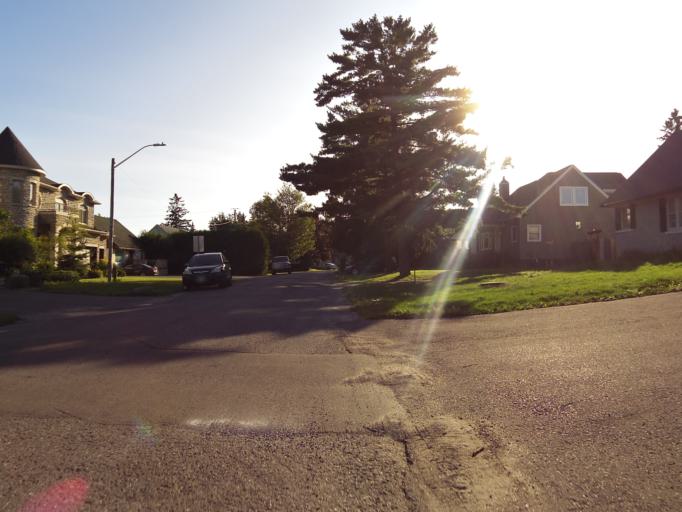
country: CA
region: Ontario
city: Ottawa
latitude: 45.3547
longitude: -75.7124
